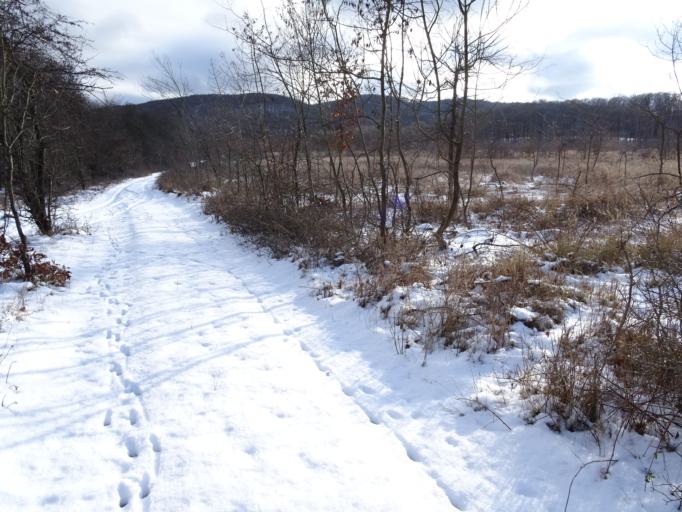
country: HU
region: Komarom-Esztergom
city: Oroszlany
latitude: 47.4739
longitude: 18.3775
